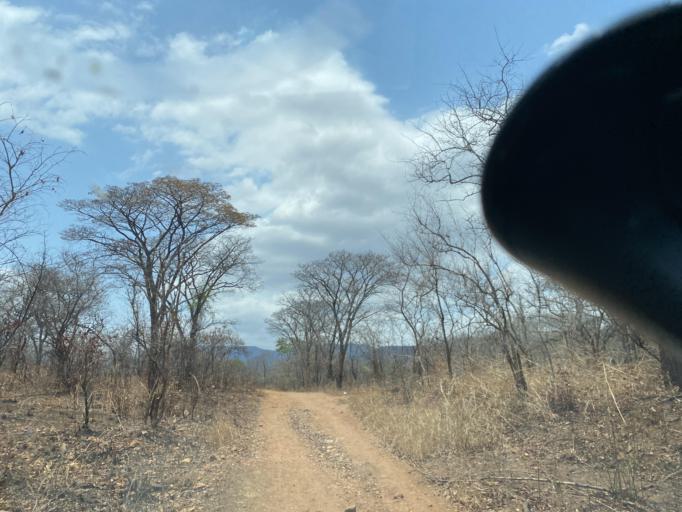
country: ZM
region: Lusaka
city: Luangwa
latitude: -15.1783
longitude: 29.7137
